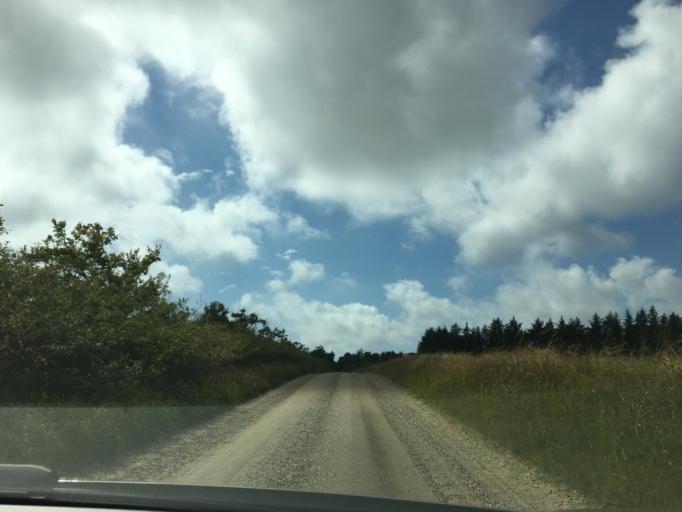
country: DK
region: South Denmark
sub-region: Varde Kommune
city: Oksbol
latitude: 55.7406
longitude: 8.2458
